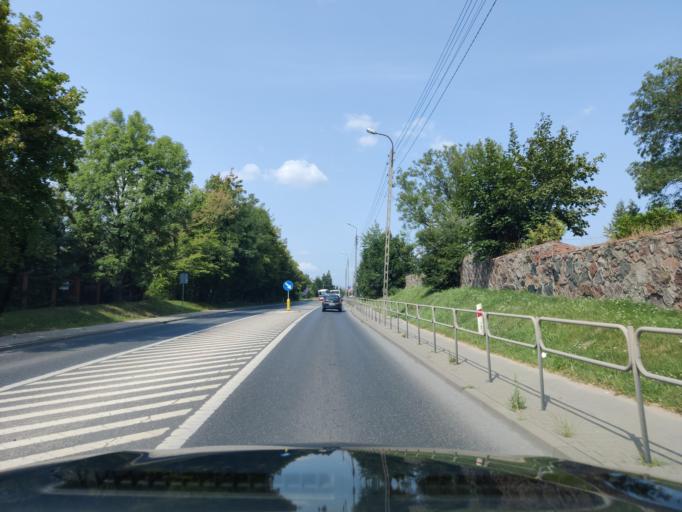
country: PL
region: Masovian Voivodeship
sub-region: Powiat pultuski
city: Pultusk
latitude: 52.7171
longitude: 21.0844
